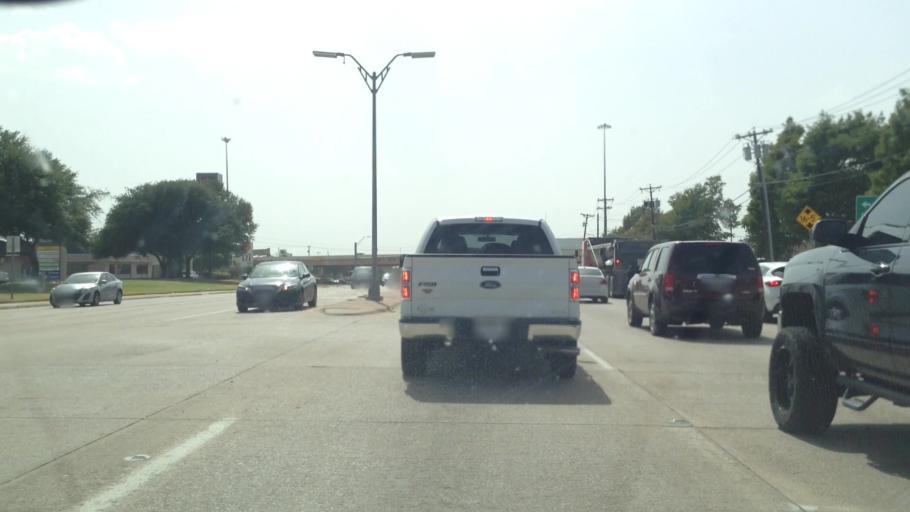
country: US
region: Texas
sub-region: Collin County
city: McKinney
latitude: 33.2167
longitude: -96.6334
